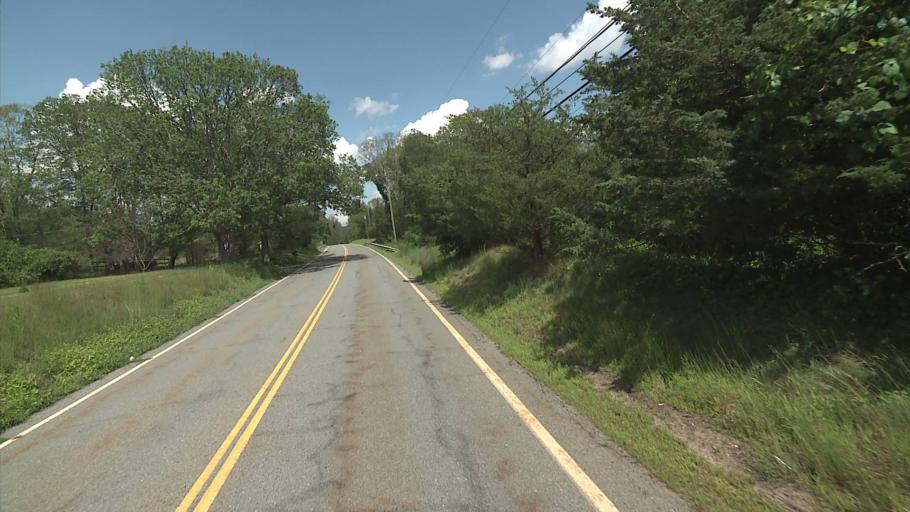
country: US
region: Connecticut
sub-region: Tolland County
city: Mansfield City
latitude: 41.7895
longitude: -72.1772
